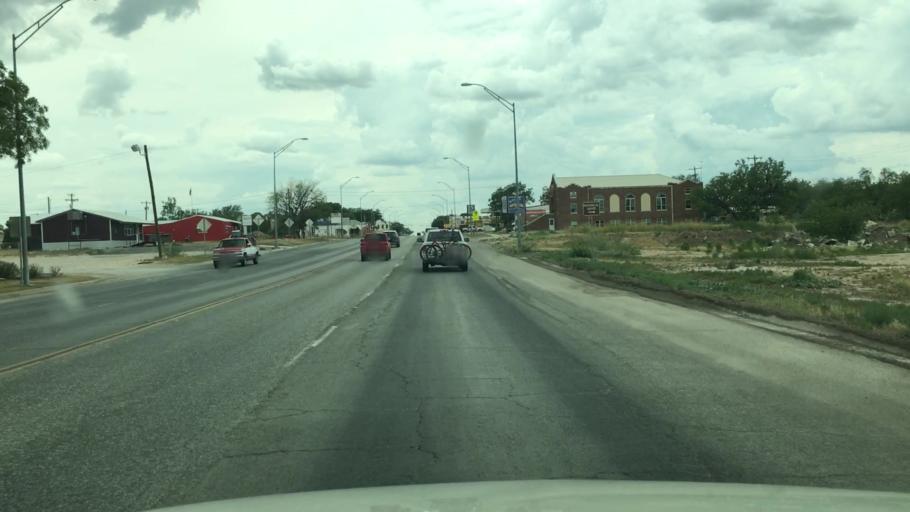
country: US
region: Texas
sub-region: Sterling County
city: Sterling City
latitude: 31.8364
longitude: -100.9834
